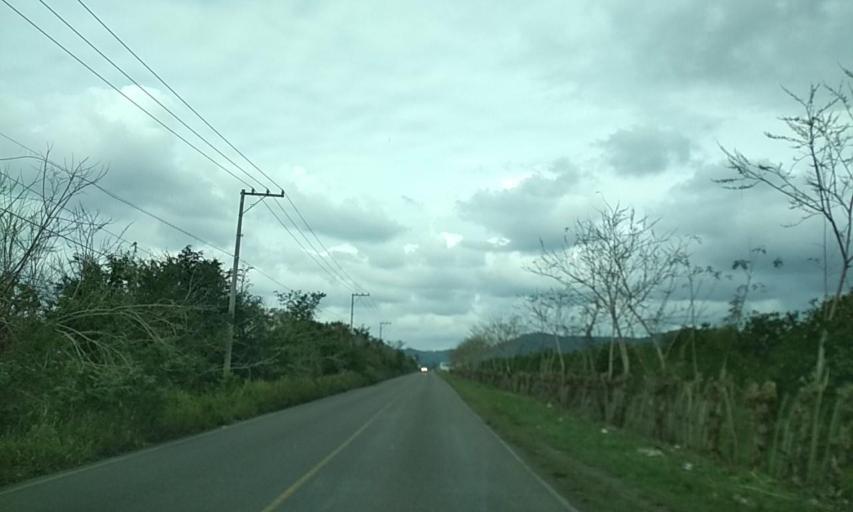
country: MX
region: Veracruz
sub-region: Papantla
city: El Chote
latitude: 20.3871
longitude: -97.3366
